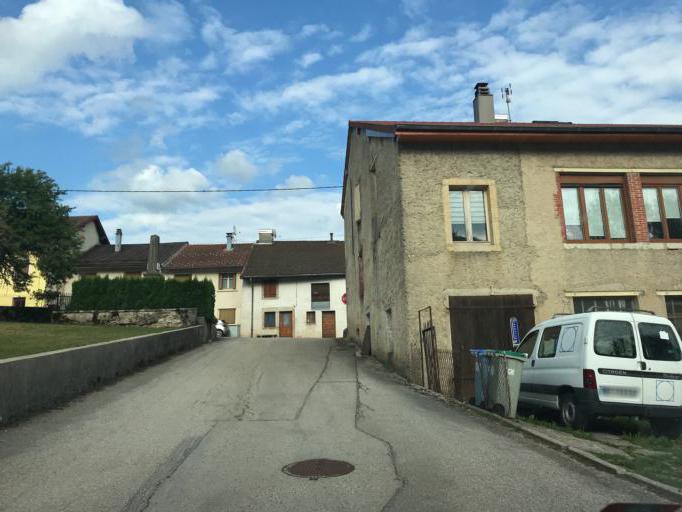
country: FR
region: Franche-Comte
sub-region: Departement du Jura
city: Saint-Lupicin
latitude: 46.4250
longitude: 5.8020
